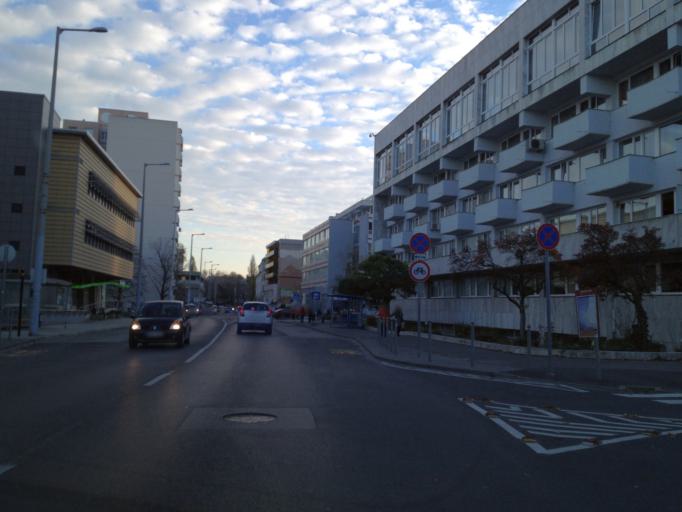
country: HU
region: Gyor-Moson-Sopron
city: Gyor
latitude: 47.6875
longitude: 17.6363
